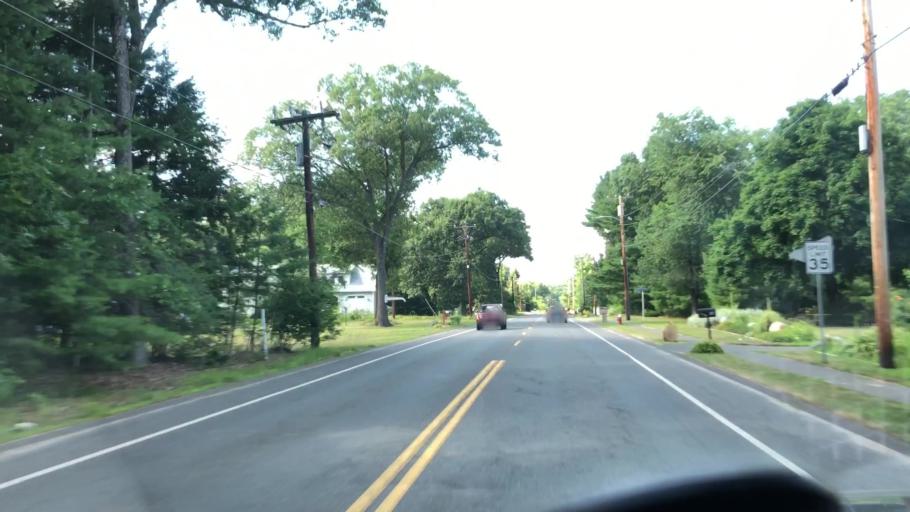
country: US
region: Massachusetts
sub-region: Hampshire County
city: Southampton
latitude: 42.2068
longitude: -72.6894
